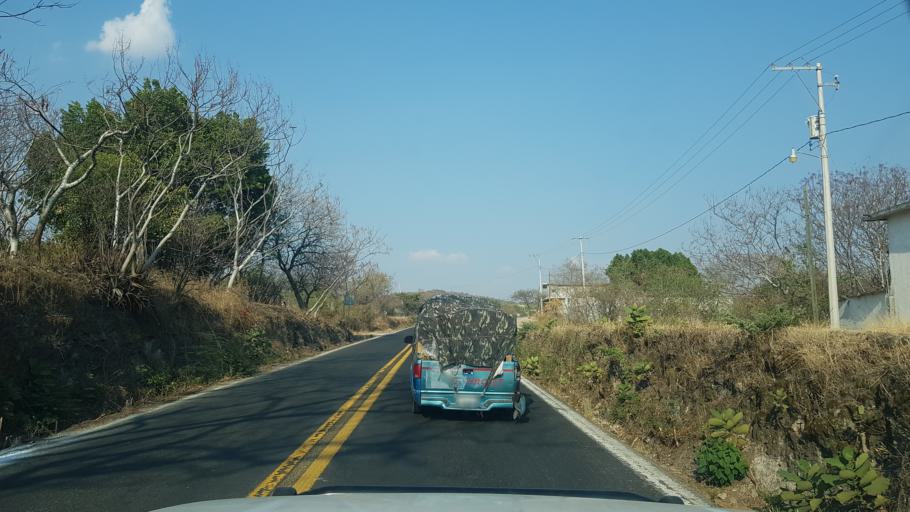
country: MX
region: Puebla
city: Calmeca
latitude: 18.6433
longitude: -98.6348
